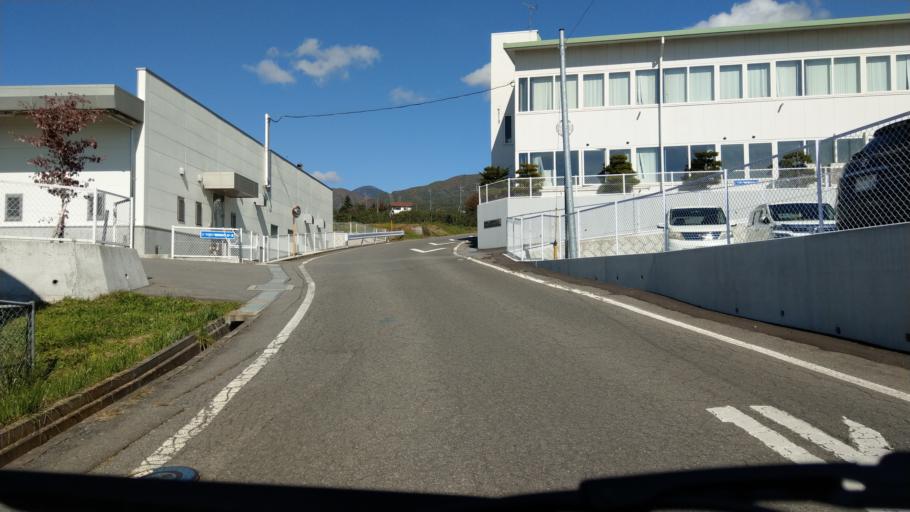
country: JP
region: Nagano
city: Komoro
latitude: 36.3532
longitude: 138.4017
